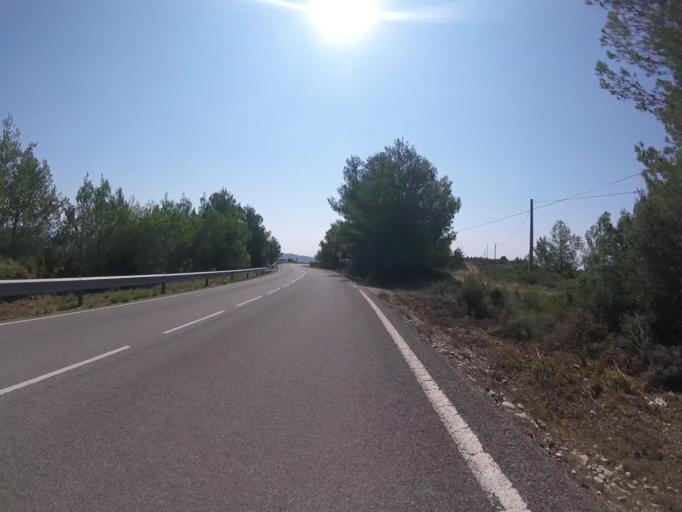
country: ES
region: Valencia
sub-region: Provincia de Castello
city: Benafigos
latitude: 40.2442
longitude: -0.1940
